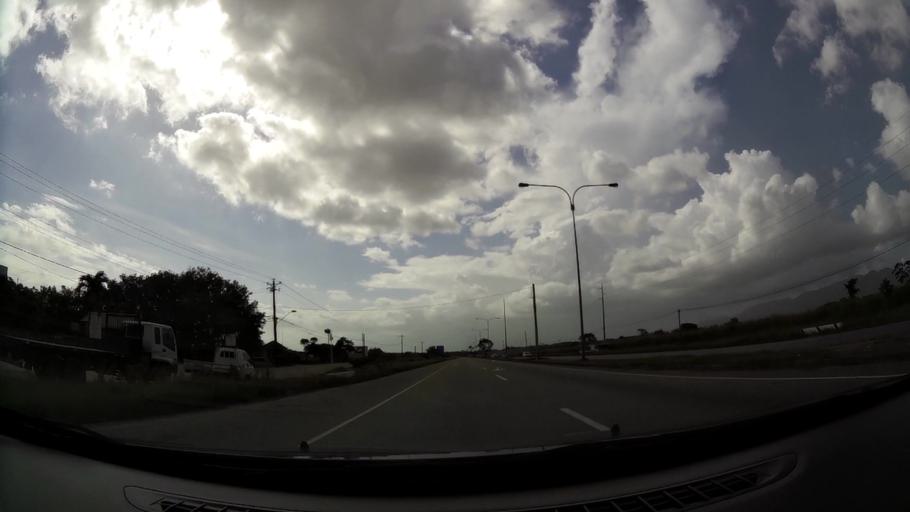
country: TT
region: Tunapuna/Piarco
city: Arouca
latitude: 10.6148
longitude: -61.3282
